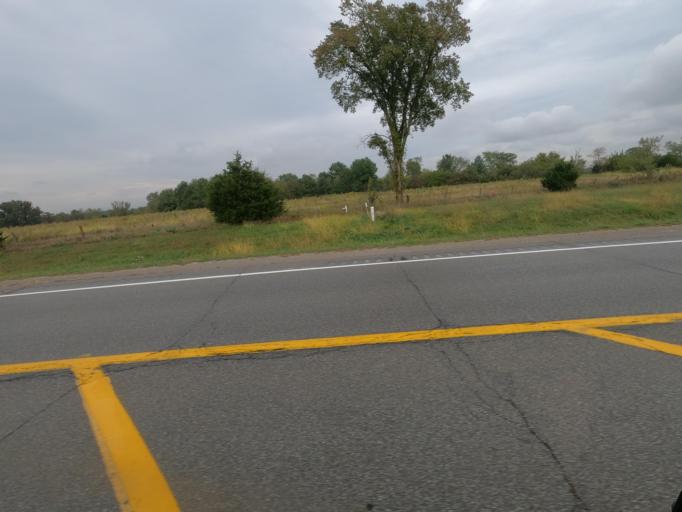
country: US
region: Iowa
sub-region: Van Buren County
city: Keosauqua
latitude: 40.8094
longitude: -91.9311
